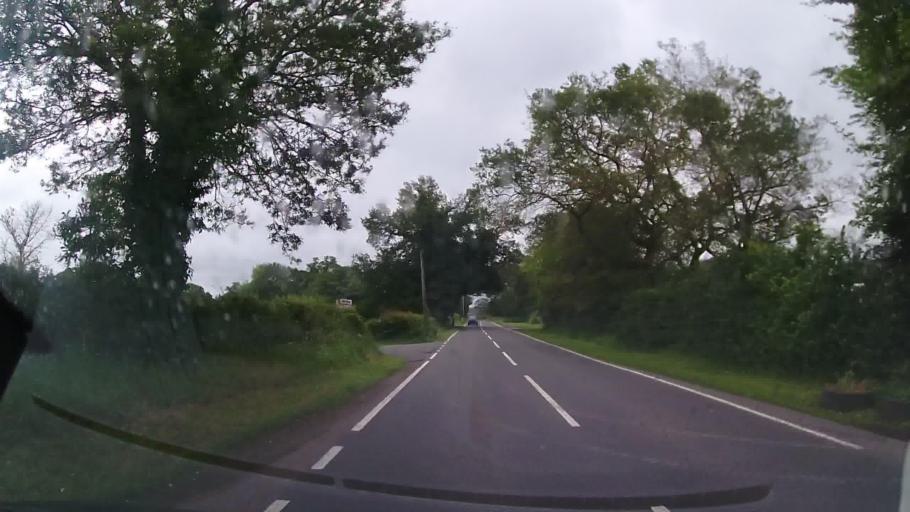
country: GB
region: England
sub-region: Shropshire
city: Prees
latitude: 52.8813
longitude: -2.6541
